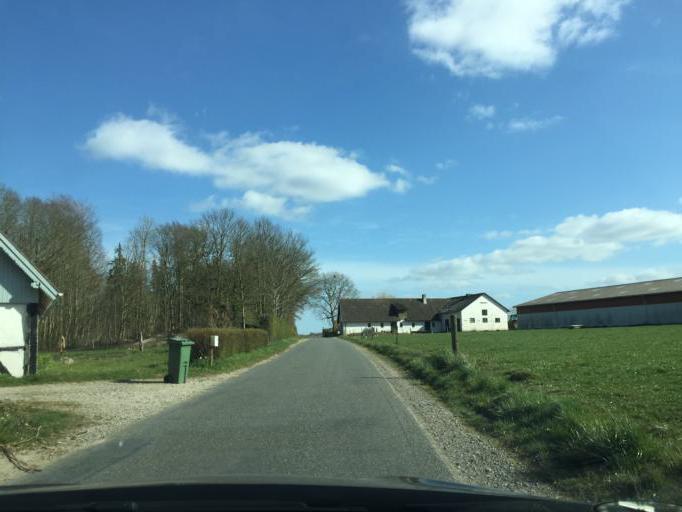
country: DK
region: South Denmark
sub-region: Faaborg-Midtfyn Kommune
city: Arslev
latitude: 55.2970
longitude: 10.5003
